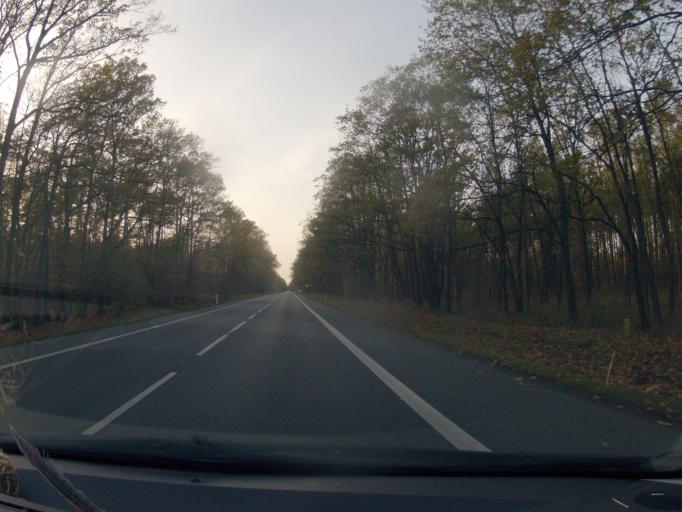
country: PL
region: Opole Voivodeship
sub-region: Powiat opolski
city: Chrzastowice
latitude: 50.6278
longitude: 18.0354
